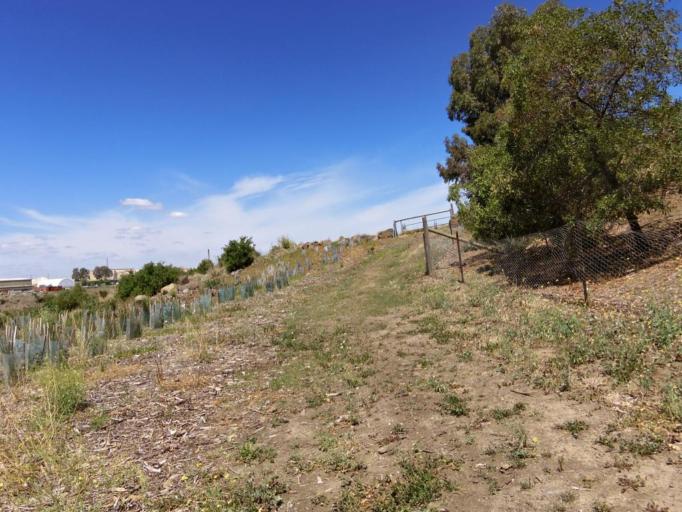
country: AU
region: Victoria
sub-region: Hume
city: Campbellfield
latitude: -37.6813
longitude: 144.9711
